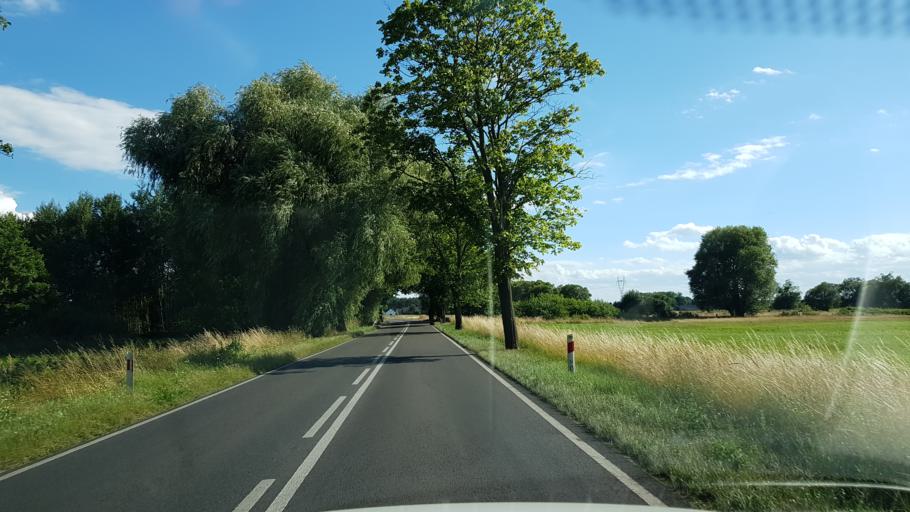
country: PL
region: West Pomeranian Voivodeship
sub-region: Powiat goleniowski
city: Goleniow
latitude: 53.5873
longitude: 14.7399
